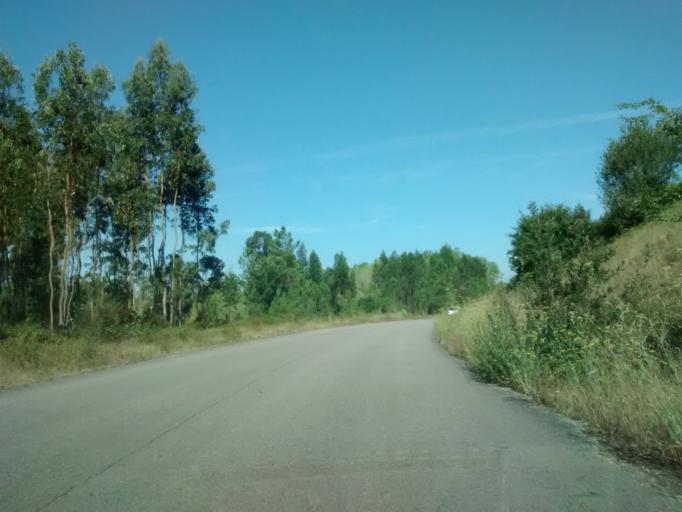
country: PT
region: Coimbra
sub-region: Cantanhede
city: Cantanhede
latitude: 40.4244
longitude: -8.6203
